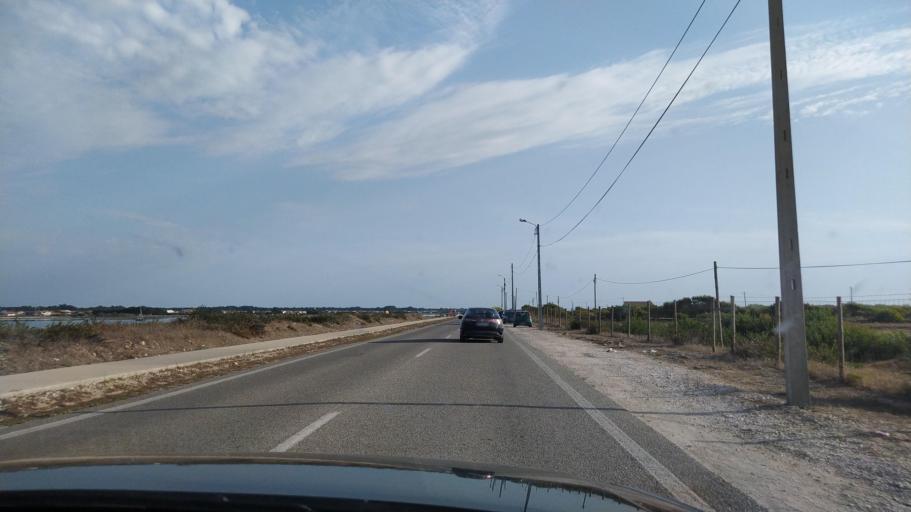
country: PT
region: Aveiro
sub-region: Ilhavo
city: Gafanha da Encarnacao
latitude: 40.6051
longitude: -8.7488
